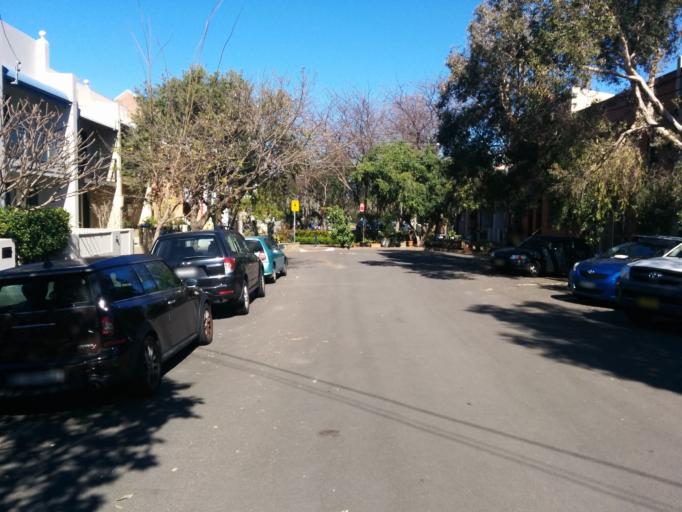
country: AU
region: New South Wales
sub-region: City of Sydney
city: Alexandria
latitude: -33.9035
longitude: 151.1920
